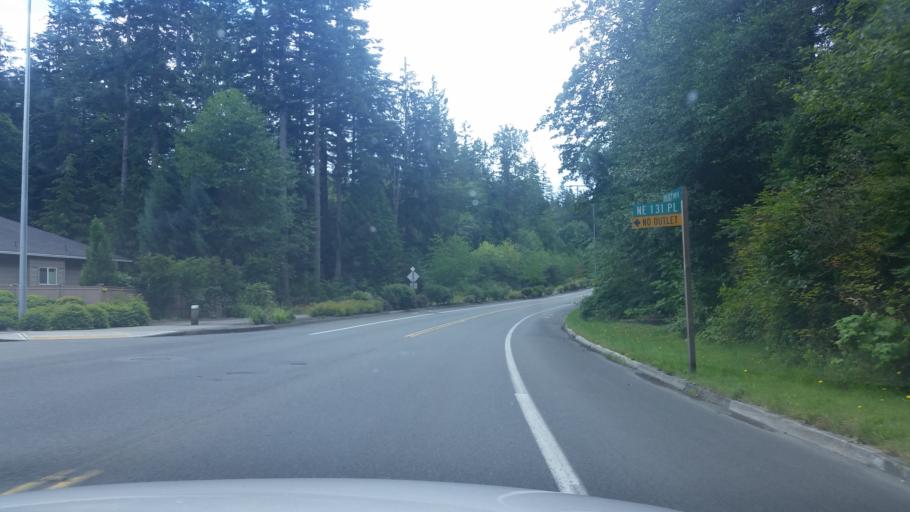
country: US
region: Washington
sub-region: King County
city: Union Hill-Novelty Hill
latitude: 47.7164
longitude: -122.0272
